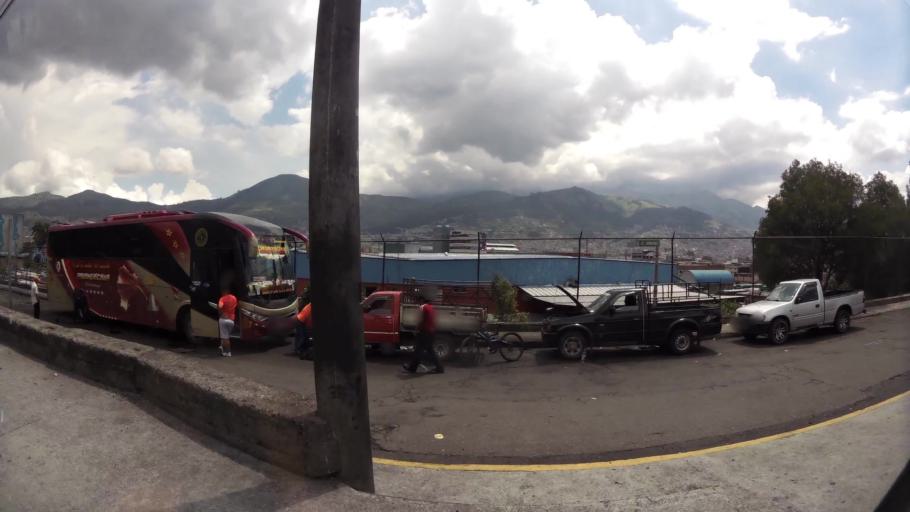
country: EC
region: Pichincha
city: Quito
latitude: -0.2532
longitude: -78.5202
